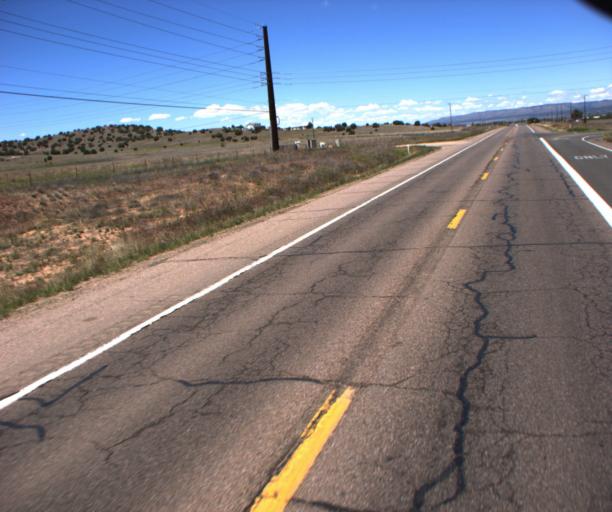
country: US
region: Arizona
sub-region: Yavapai County
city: Paulden
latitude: 34.8335
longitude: -112.4608
